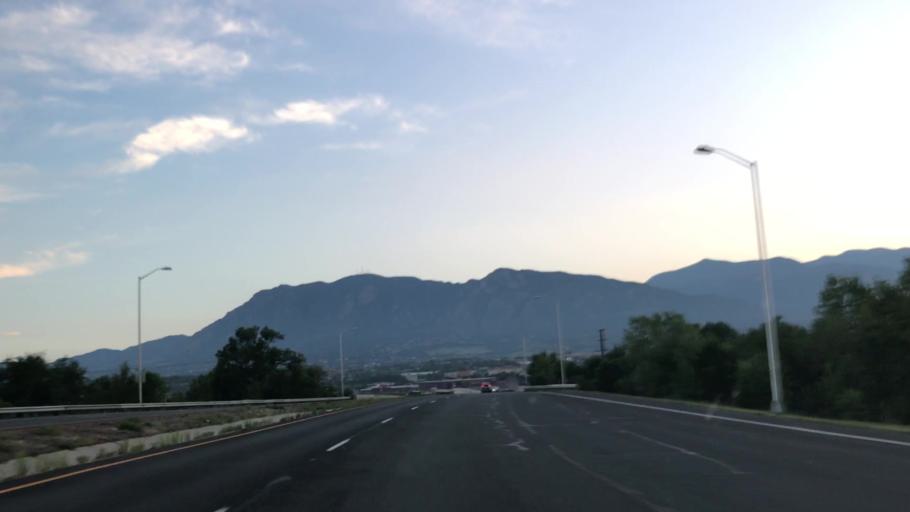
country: US
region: Colorado
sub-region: El Paso County
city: Stratmoor
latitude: 38.7991
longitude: -104.7824
